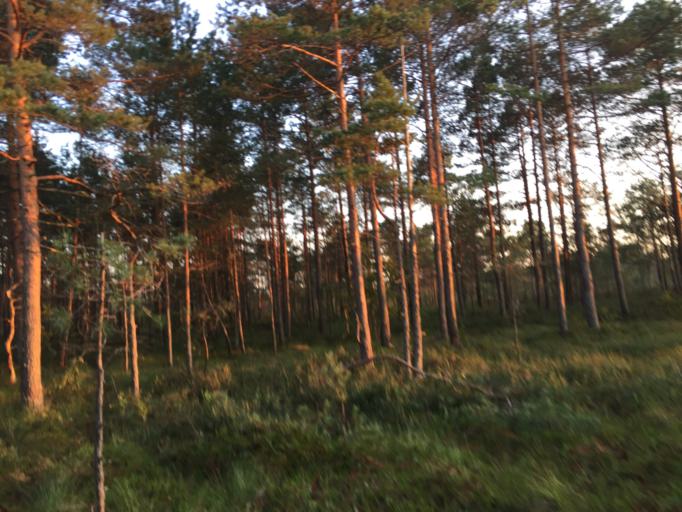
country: LV
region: Limbazu Rajons
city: Limbazi
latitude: 57.5732
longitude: 24.7876
